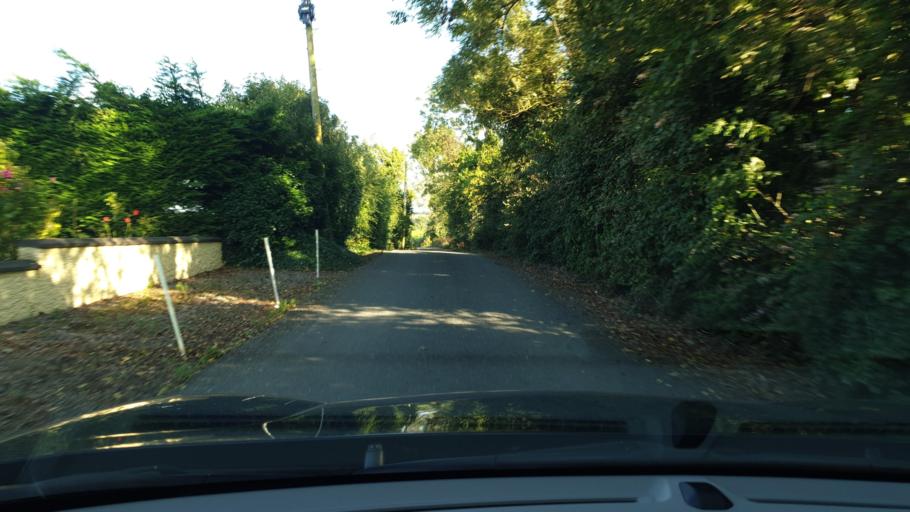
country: IE
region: Leinster
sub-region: An Mhi
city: Stamullin
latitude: 53.5896
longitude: -6.2575
